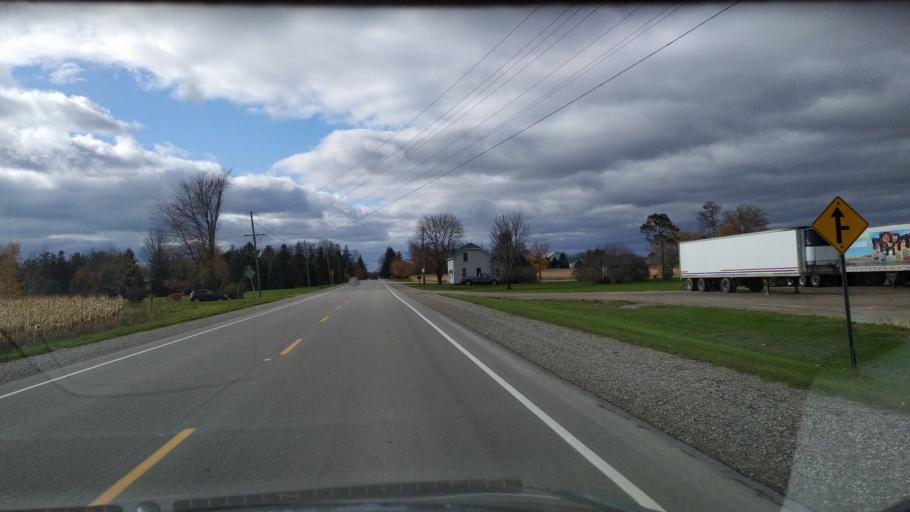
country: CA
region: Ontario
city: Stratford
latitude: 43.2642
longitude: -81.1013
